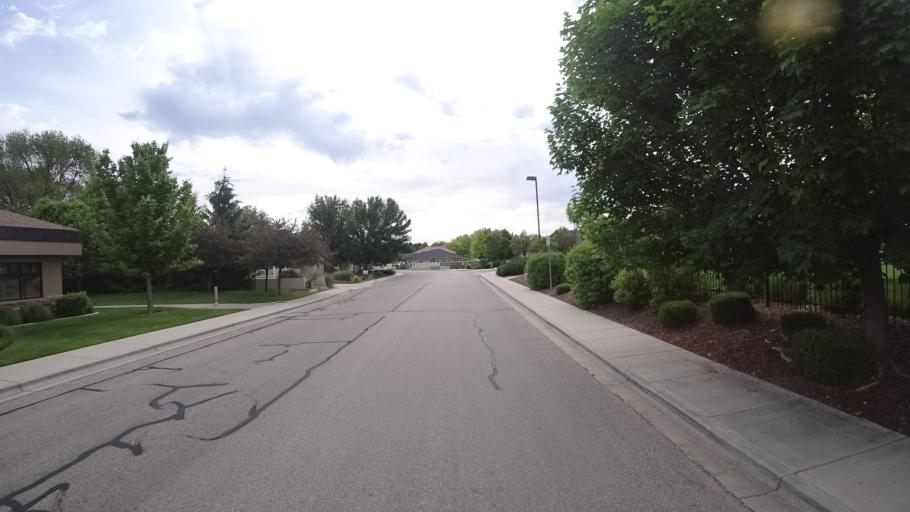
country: US
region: Idaho
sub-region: Ada County
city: Meridian
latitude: 43.5860
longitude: -116.3920
